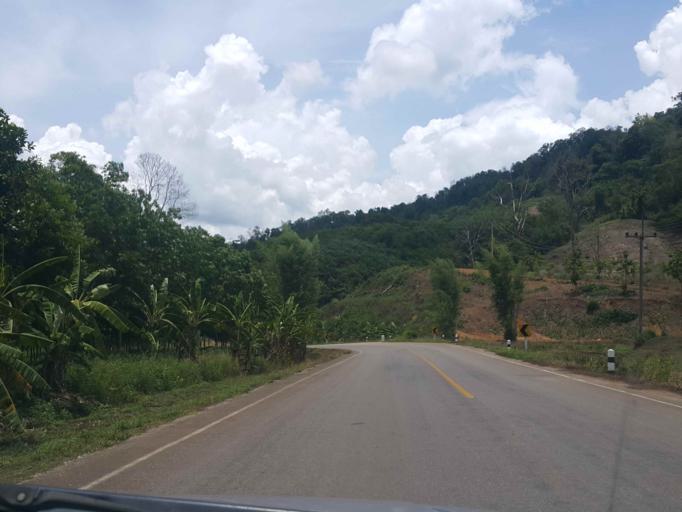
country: TH
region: Phayao
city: Chiang Muan
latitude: 18.9099
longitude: 100.1172
